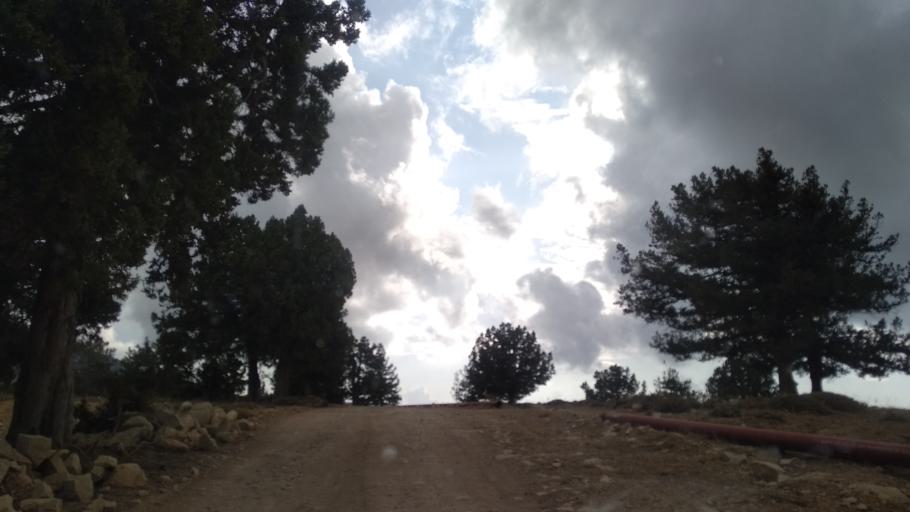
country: TR
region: Mersin
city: Sarikavak
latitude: 36.5667
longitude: 33.7404
